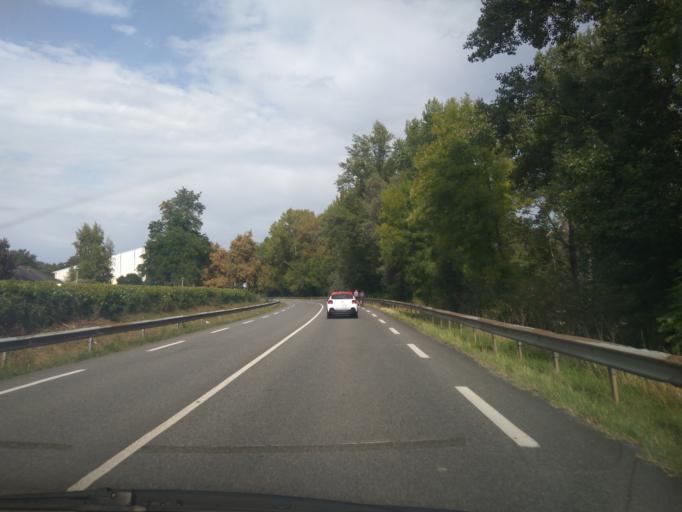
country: FR
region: Aquitaine
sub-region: Departement des Pyrenees-Atlantiques
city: Artiguelouve
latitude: 43.3062
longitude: -0.4418
